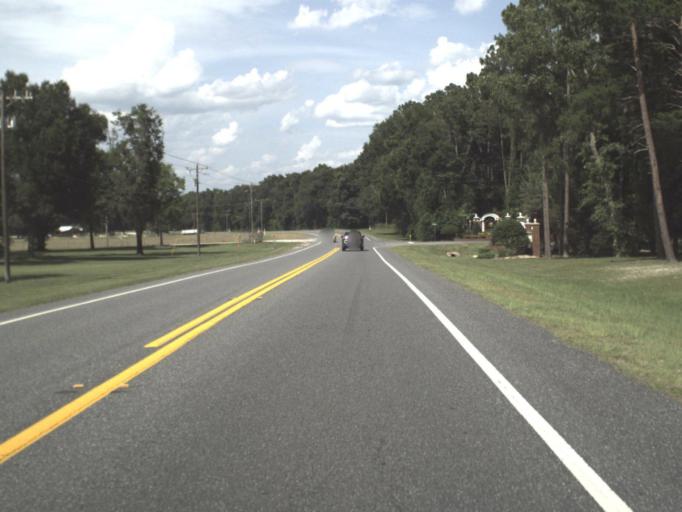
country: US
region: Florida
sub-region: Columbia County
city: Lake City
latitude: 30.0961
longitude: -82.6714
